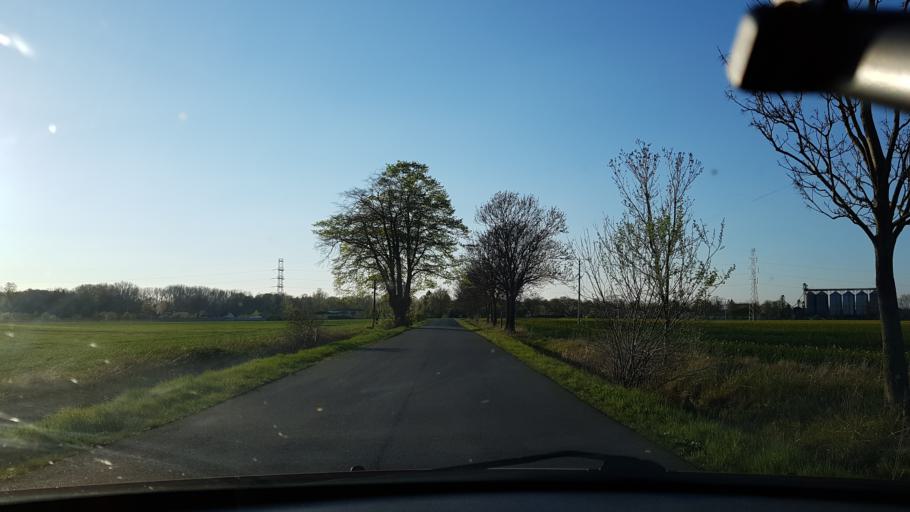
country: PL
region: Opole Voivodeship
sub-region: Powiat nyski
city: Nysa
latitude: 50.4257
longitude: 17.3108
